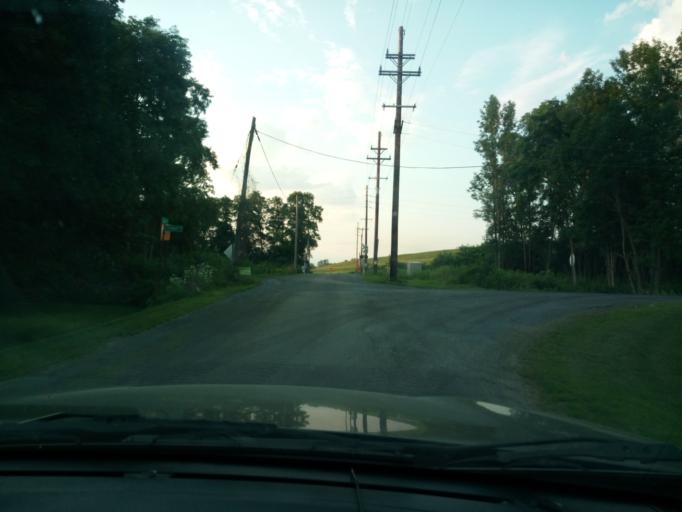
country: US
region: New York
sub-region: Wayne County
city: Clyde
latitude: 43.0653
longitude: -76.8324
